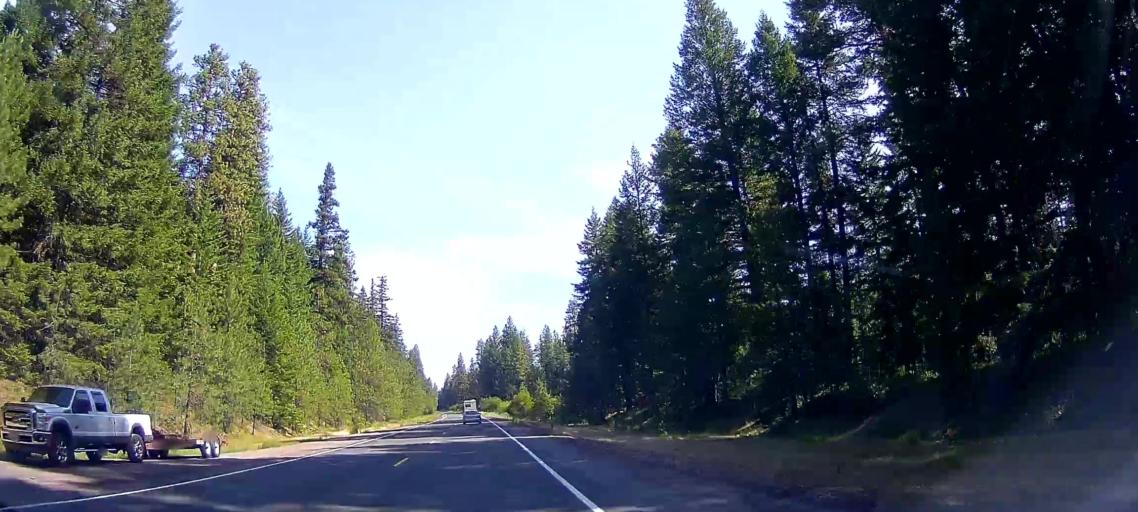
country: US
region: Oregon
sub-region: Jefferson County
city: Warm Springs
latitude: 45.0357
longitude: -121.5108
